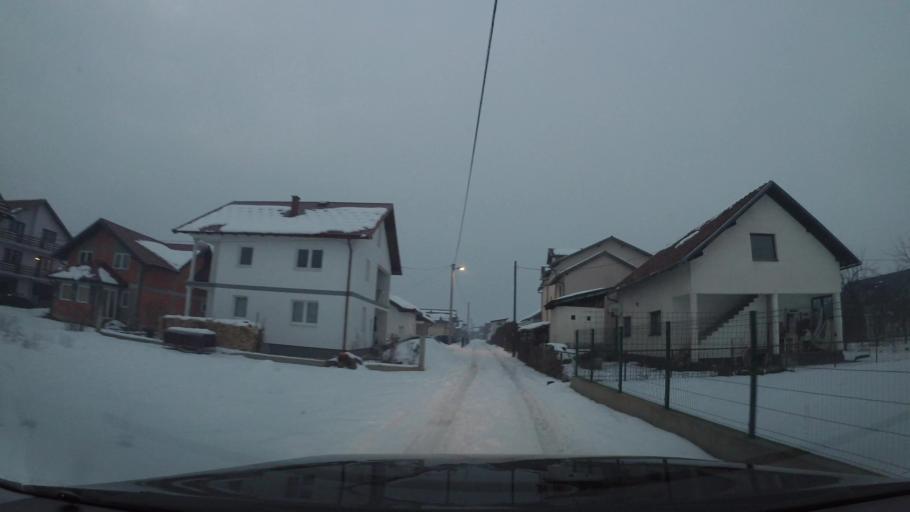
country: BA
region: Federation of Bosnia and Herzegovina
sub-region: Kanton Sarajevo
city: Sarajevo
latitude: 43.8543
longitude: 18.2920
